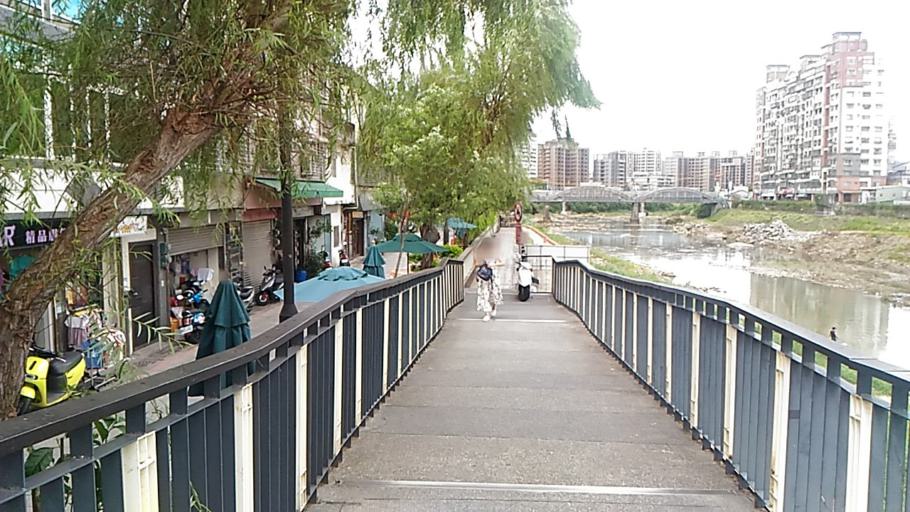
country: TW
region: Taiwan
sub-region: Taoyuan
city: Taoyuan
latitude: 24.9336
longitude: 121.3712
